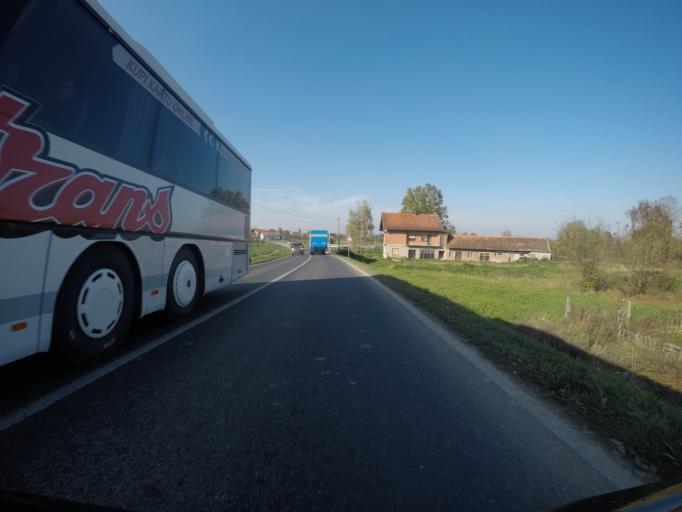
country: HR
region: Bjelovarsko-Bilogorska
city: Predavac
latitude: 45.9320
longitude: 16.7848
